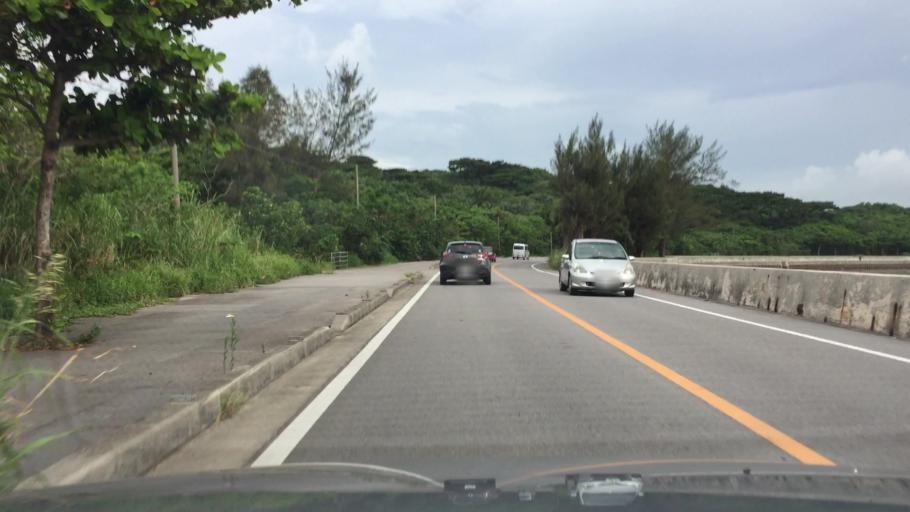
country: JP
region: Okinawa
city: Ishigaki
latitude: 24.4319
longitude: 124.1244
